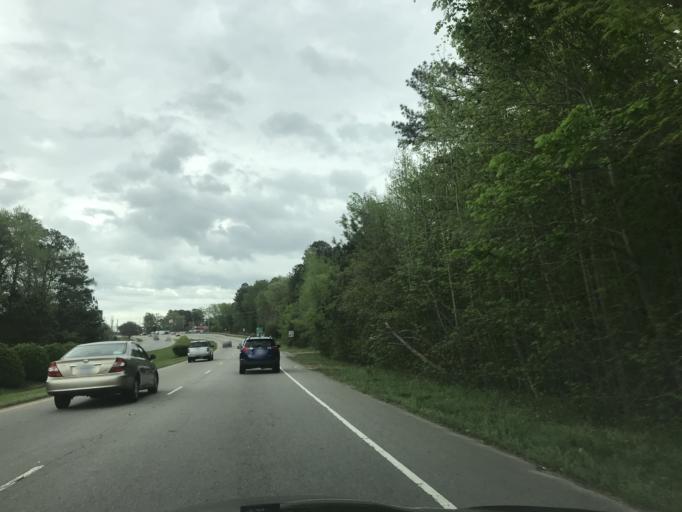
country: US
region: North Carolina
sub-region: Wake County
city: Knightdale
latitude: 35.7956
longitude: -78.5248
